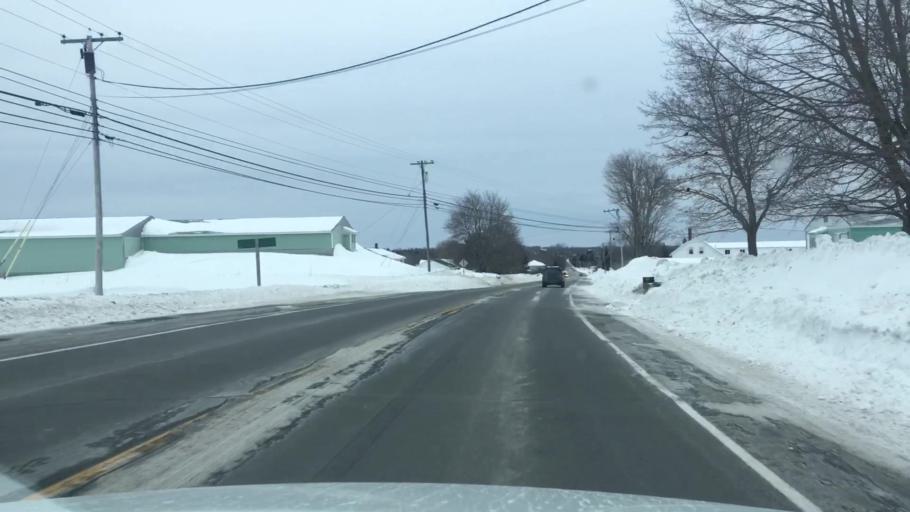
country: US
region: Maine
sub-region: Penobscot County
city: Charleston
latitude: 45.0269
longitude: -69.0305
